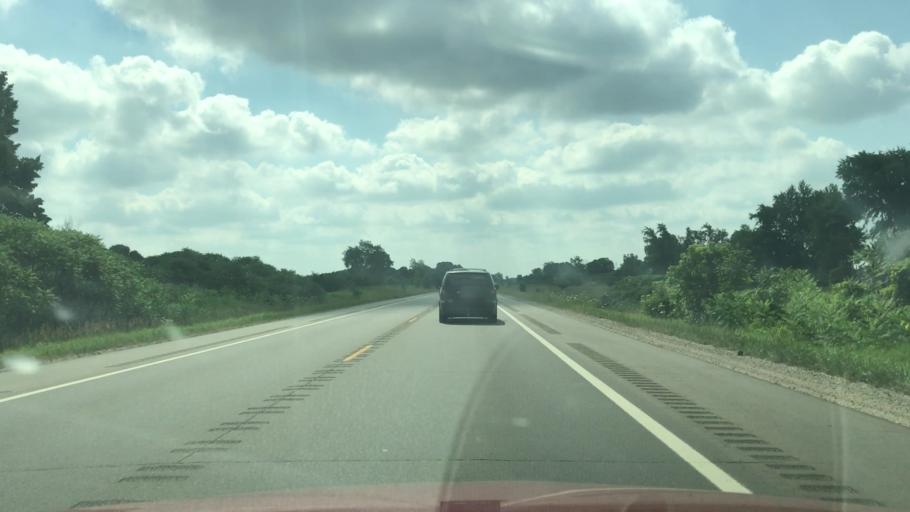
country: US
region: Michigan
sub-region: Kent County
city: Kent City
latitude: 43.2269
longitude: -85.7809
